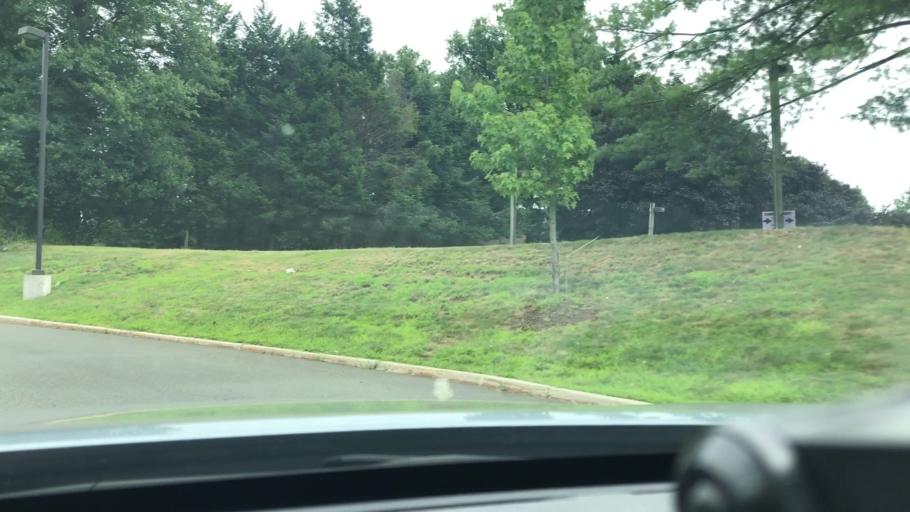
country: US
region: New York
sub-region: Rockland County
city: Blauvelt
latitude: 41.0805
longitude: -73.9535
